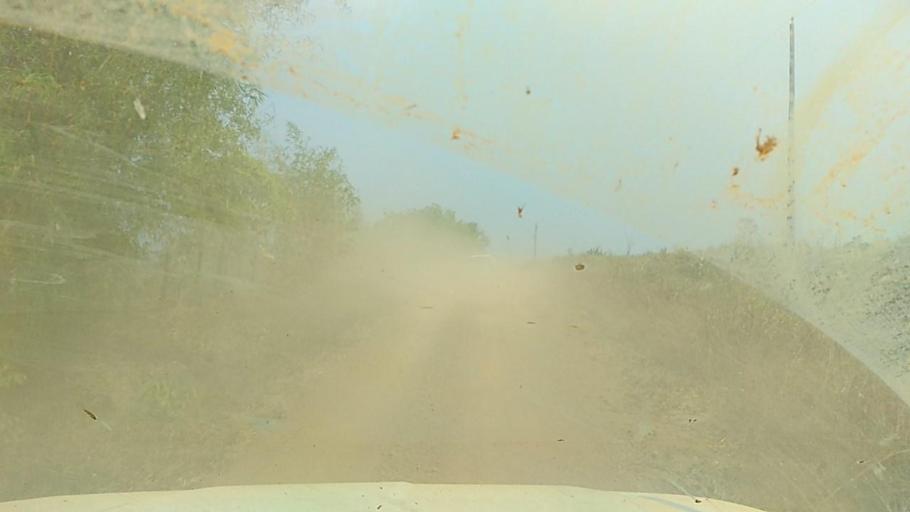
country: BR
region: Rondonia
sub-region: Porto Velho
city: Porto Velho
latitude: -8.9802
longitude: -64.3811
